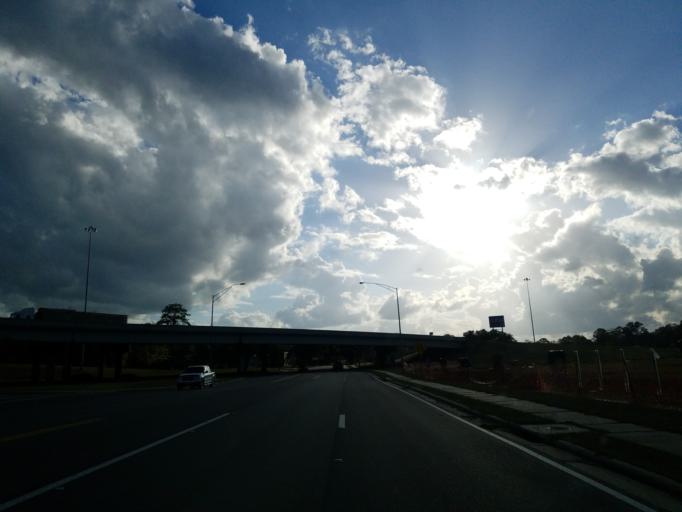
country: US
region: Mississippi
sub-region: Jones County
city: Laurel
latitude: 31.6852
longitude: -89.1379
